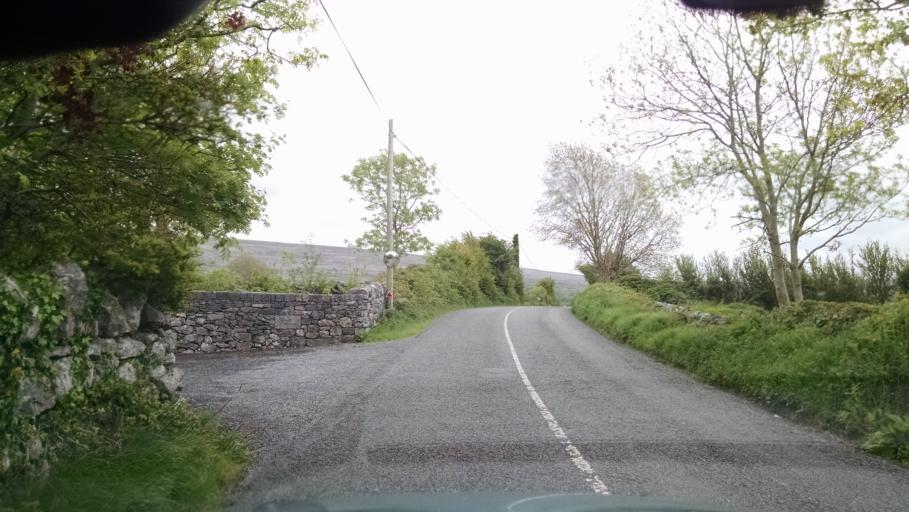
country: IE
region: Connaught
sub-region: County Galway
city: Bearna
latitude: 53.1031
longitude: -9.1597
